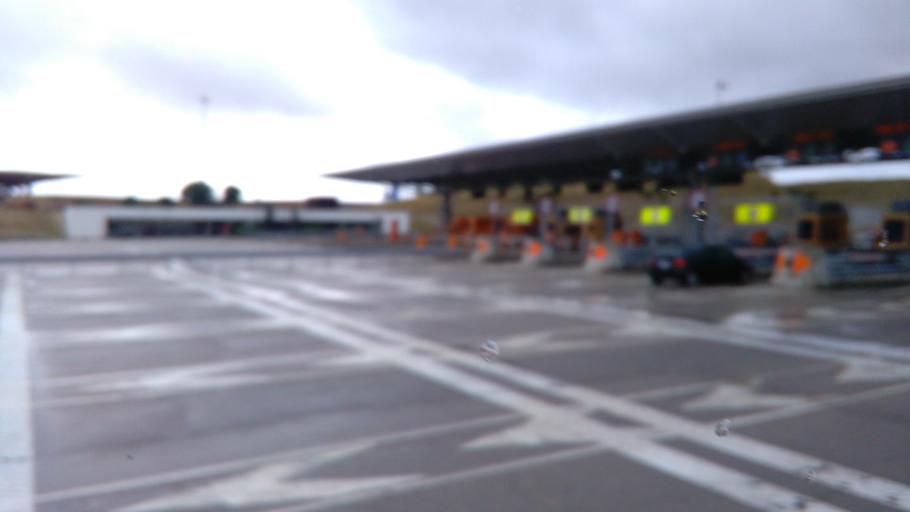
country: ES
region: Madrid
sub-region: Provincia de Madrid
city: Arroyomolinos
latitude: 40.2580
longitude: -3.9101
